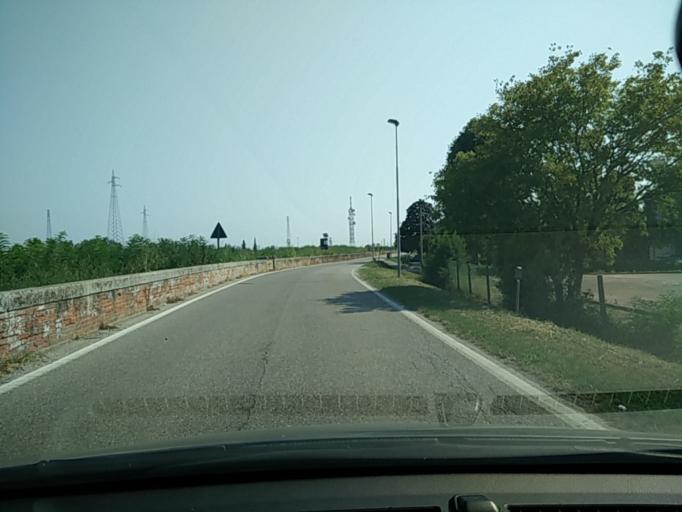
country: IT
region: Veneto
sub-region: Provincia di Venezia
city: Caorle
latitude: 45.6120
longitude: 12.8615
